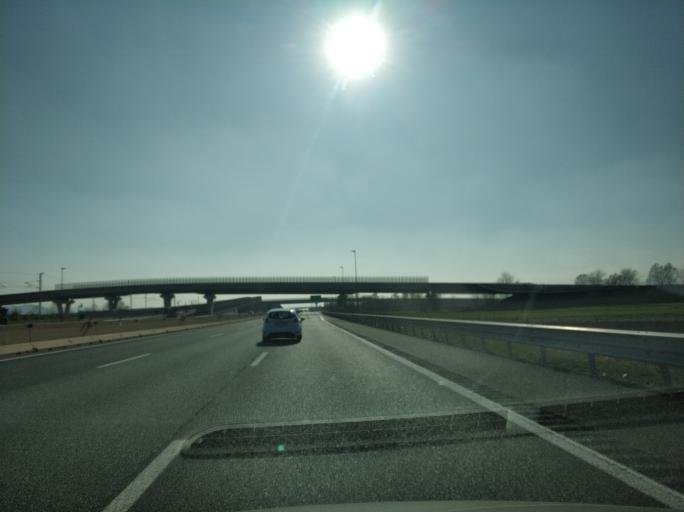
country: IT
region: Piedmont
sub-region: Provincia di Torino
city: Chivasso
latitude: 45.2248
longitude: 7.9257
